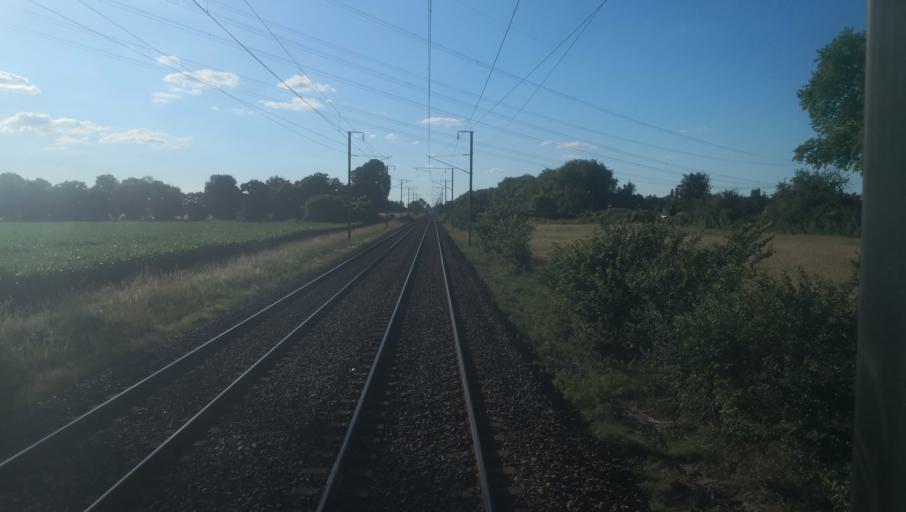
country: FR
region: Bourgogne
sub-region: Departement de la Nievre
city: Chantenay-Saint-Imbert
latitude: 46.6905
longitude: 3.2151
